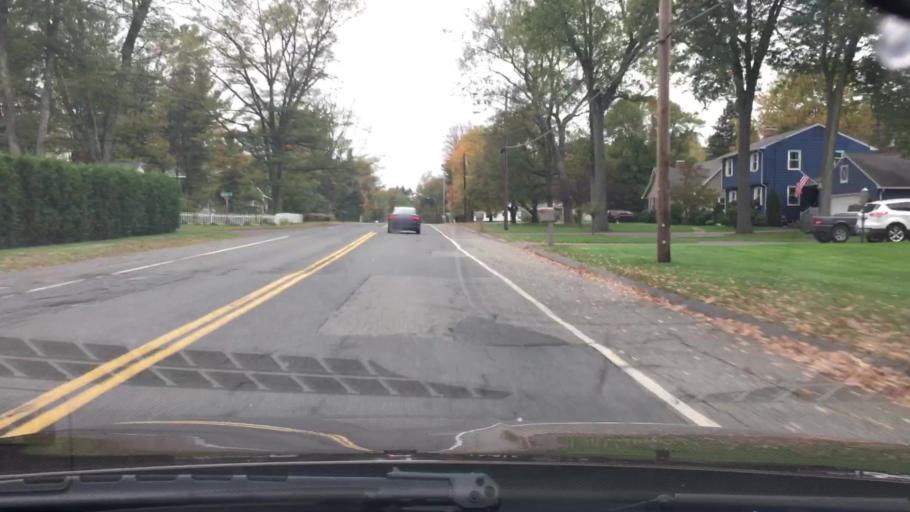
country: US
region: Massachusetts
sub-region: Hampden County
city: East Longmeadow
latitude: 42.0498
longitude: -72.4823
